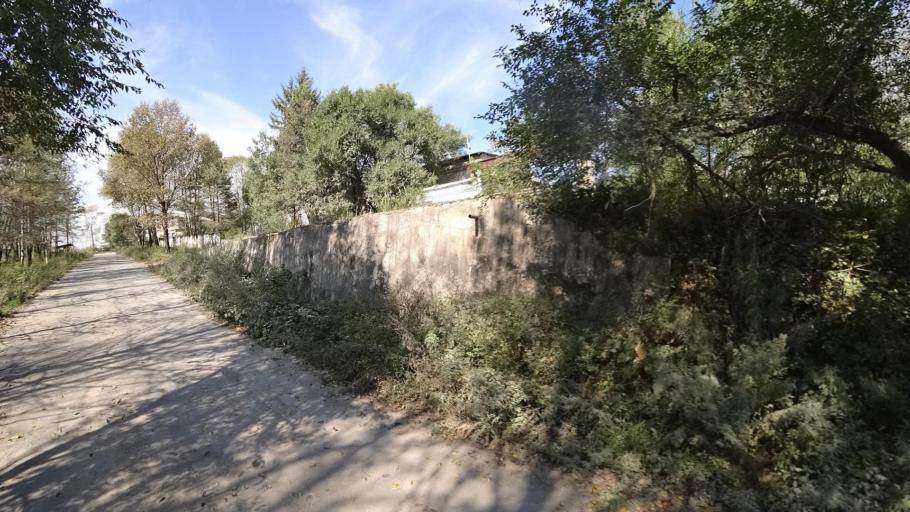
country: RU
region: Jewish Autonomous Oblast
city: Londoko
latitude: 49.0026
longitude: 131.8855
